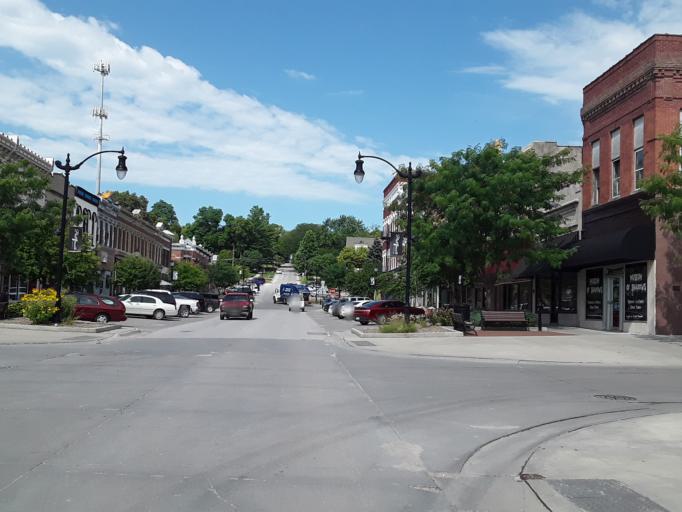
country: US
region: Nebraska
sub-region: Cass County
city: Plattsmouth
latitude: 41.0112
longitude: -95.8847
